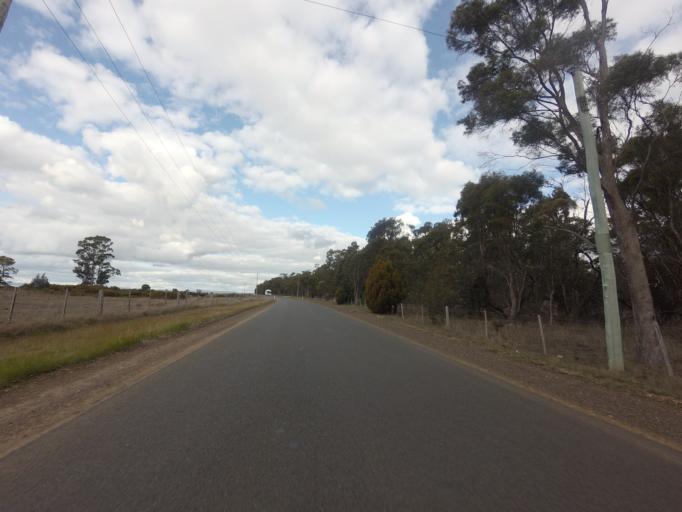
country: AU
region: Tasmania
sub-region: Northern Midlands
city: Longford
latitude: -41.8000
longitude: 147.1315
